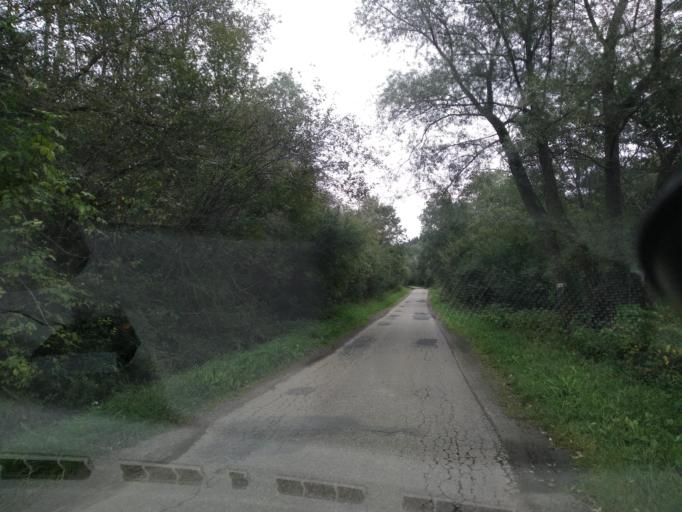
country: PL
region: Lesser Poland Voivodeship
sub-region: Powiat gorlicki
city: Uscie Gorlickie
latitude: 49.5179
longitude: 21.1547
